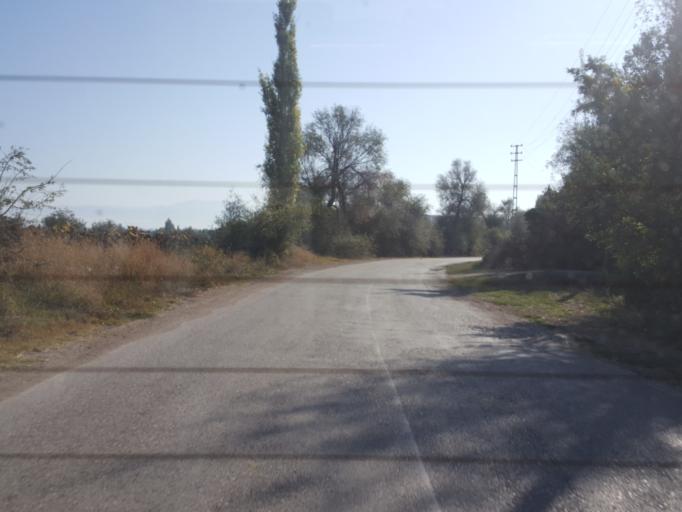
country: TR
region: Amasya
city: Saribugday
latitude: 40.7504
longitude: 35.4525
